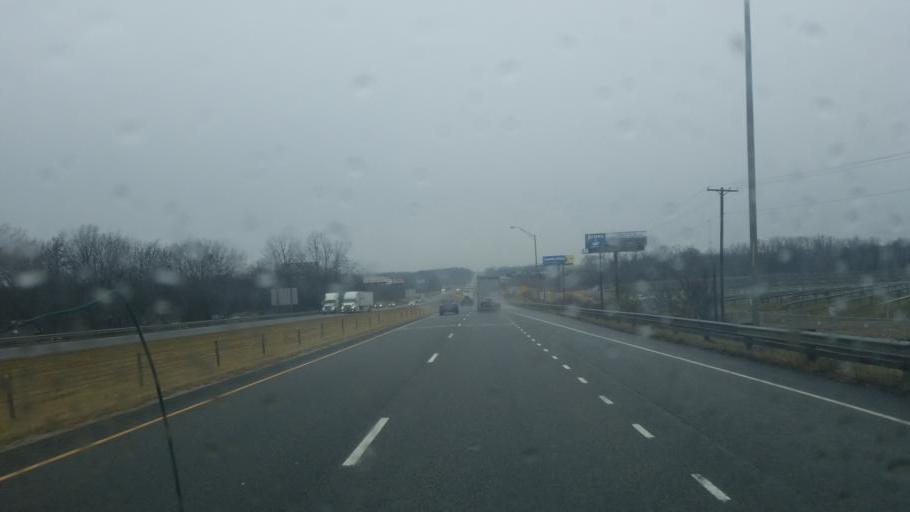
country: US
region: Ohio
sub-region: Preble County
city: New Paris
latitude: 39.8368
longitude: -84.8205
